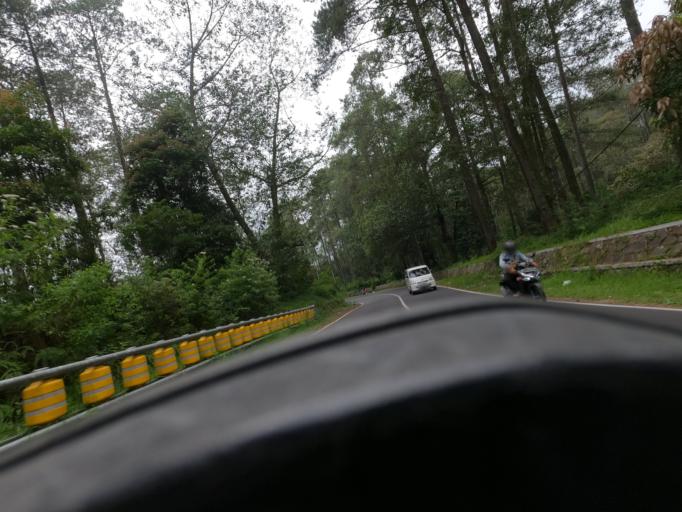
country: ID
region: West Java
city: Lembang
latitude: -6.7817
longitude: 107.6481
